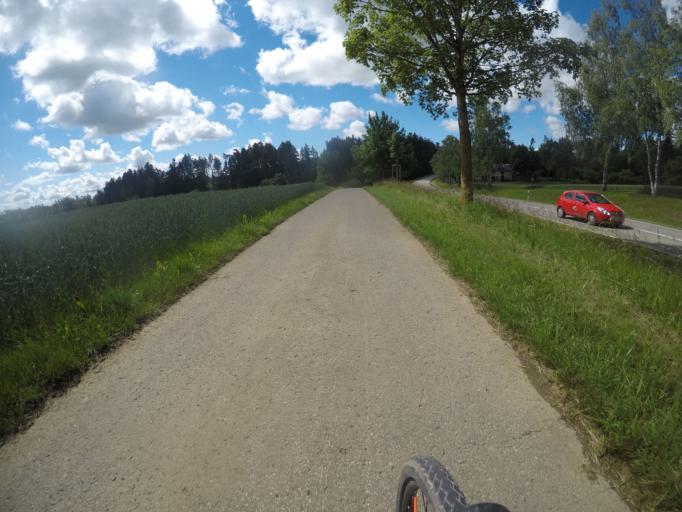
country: DE
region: Baden-Wuerttemberg
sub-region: Regierungsbezirk Stuttgart
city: Unterjettingen
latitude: 48.5508
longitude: 8.7824
